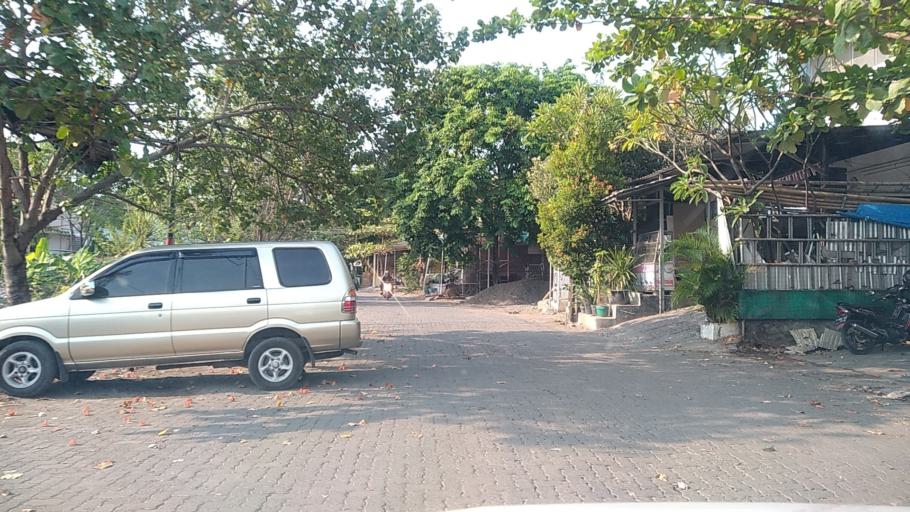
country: ID
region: Central Java
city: Semarang
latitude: -6.9600
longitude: 110.4018
